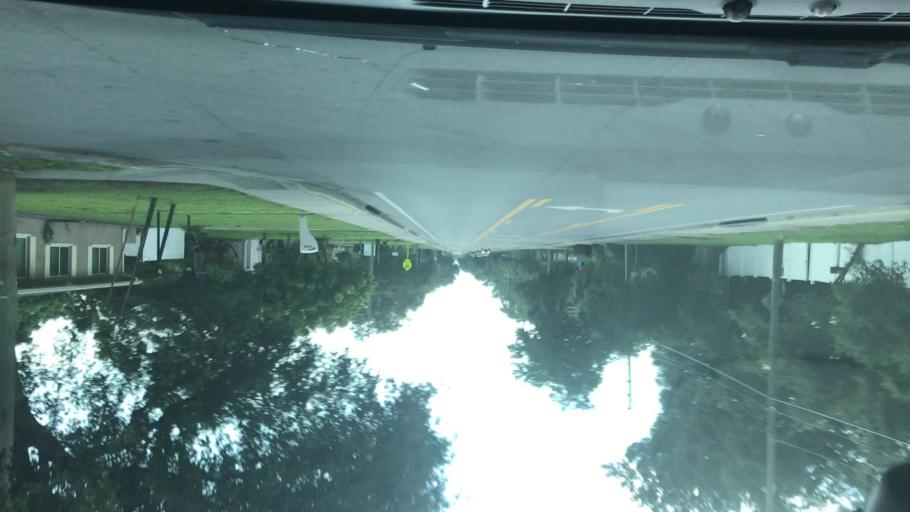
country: US
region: Florida
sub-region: Pinellas County
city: Pinellas Park
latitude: 27.8428
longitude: -82.6980
